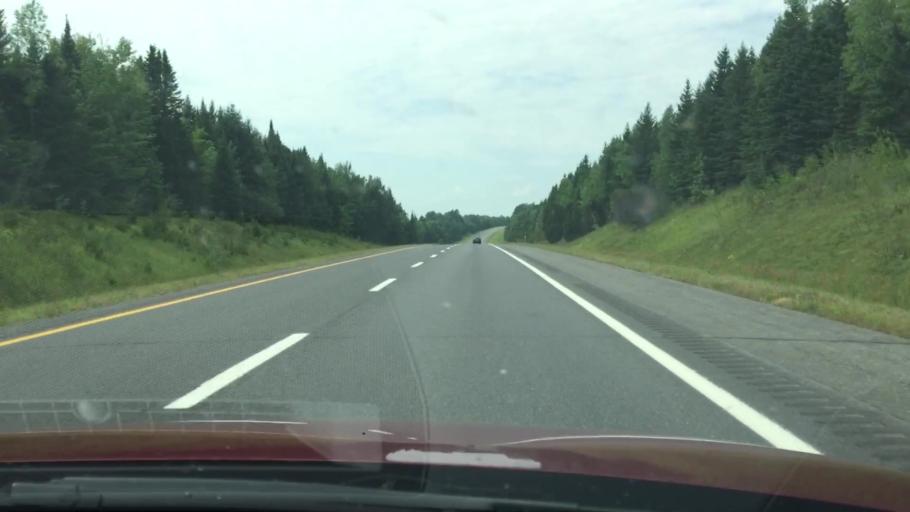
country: US
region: Maine
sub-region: Aroostook County
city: Hodgdon
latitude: 46.1407
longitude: -68.0049
